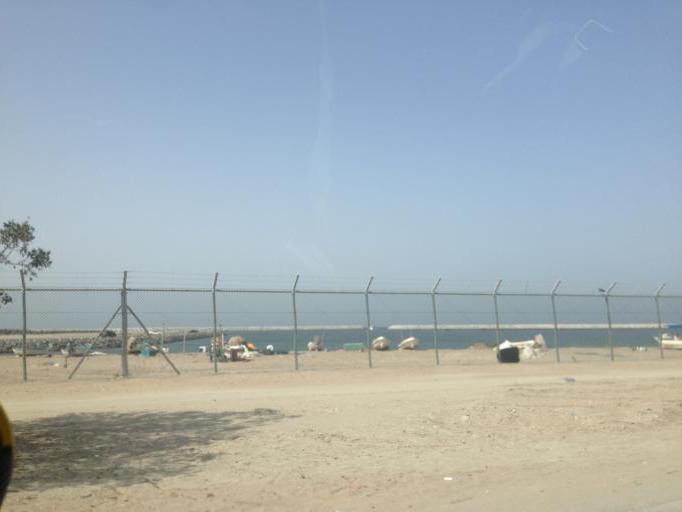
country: OM
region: Al Batinah
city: Barka'
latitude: 23.7101
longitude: 57.8908
